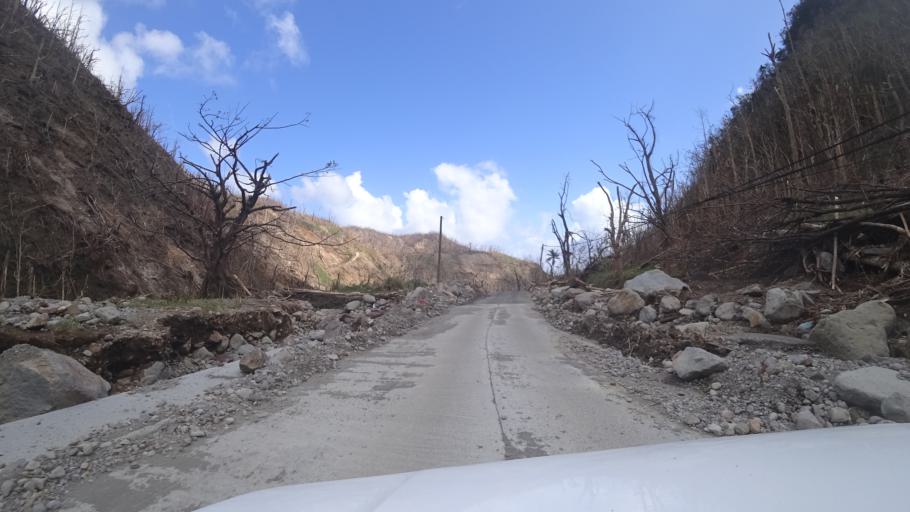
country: DM
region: Saint Patrick
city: Berekua
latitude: 15.2633
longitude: -61.3201
